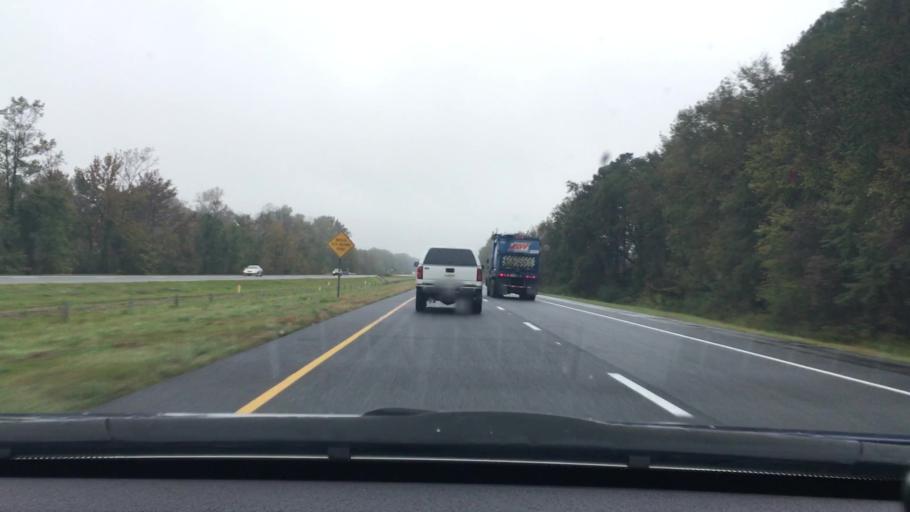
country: US
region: South Carolina
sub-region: Lee County
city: Bishopville
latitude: 34.1970
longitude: -80.1083
